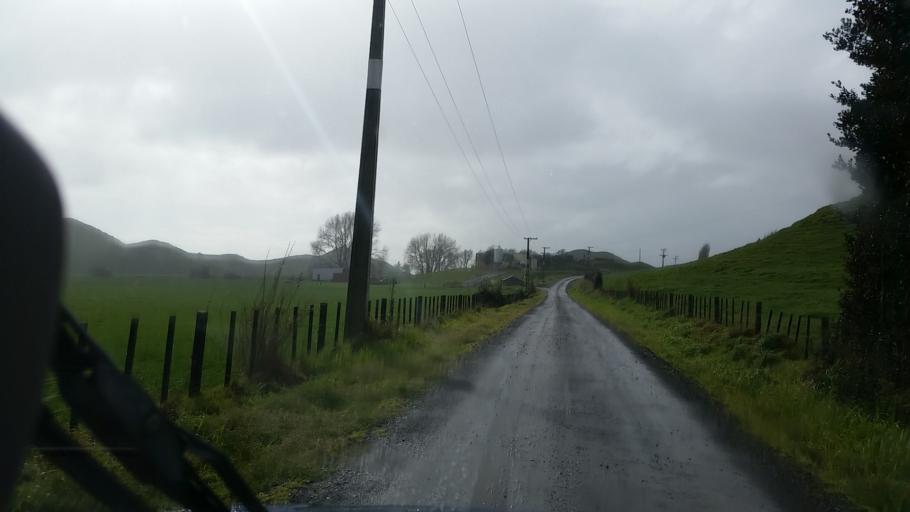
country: NZ
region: Taranaki
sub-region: South Taranaki District
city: Eltham
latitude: -39.3535
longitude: 174.4351
